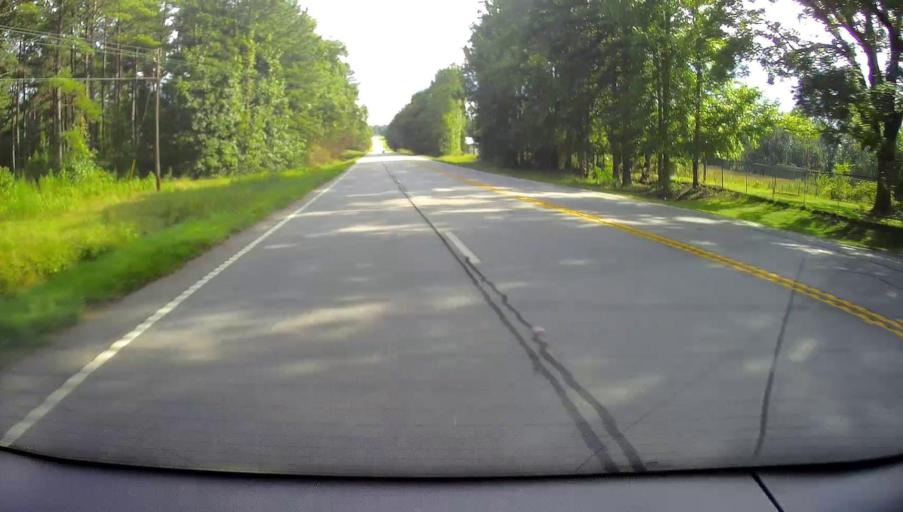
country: US
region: Georgia
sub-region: Meriwether County
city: Greenville
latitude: 33.0046
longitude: -84.5685
